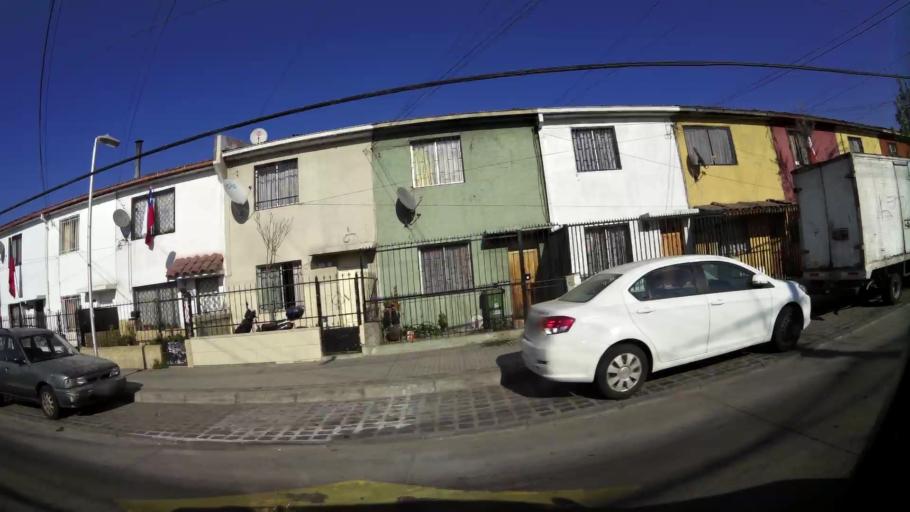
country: CL
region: Santiago Metropolitan
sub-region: Provincia de Santiago
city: Santiago
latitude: -33.4702
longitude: -70.6336
